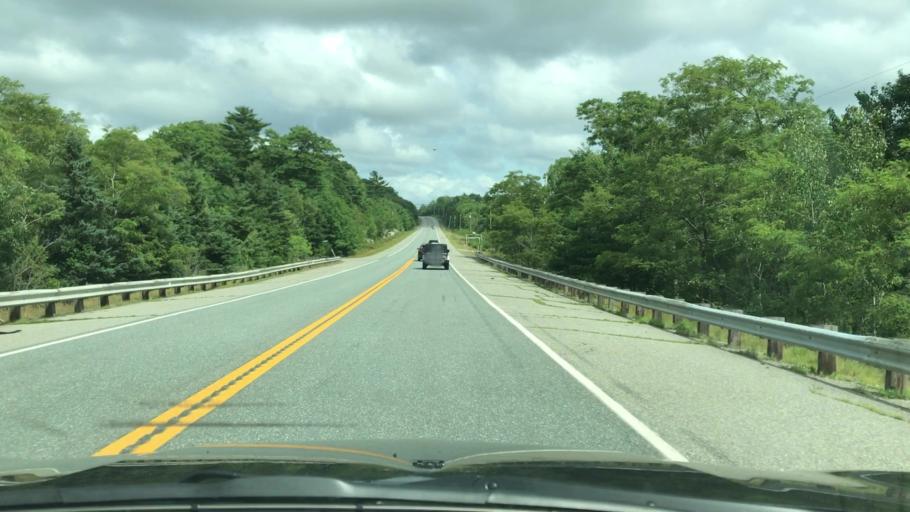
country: US
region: Maine
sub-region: Hancock County
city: Orland
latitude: 44.5661
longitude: -68.6122
